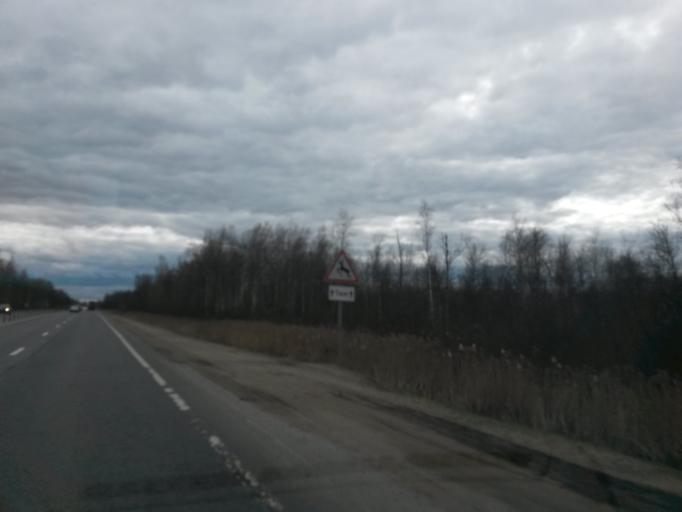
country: RU
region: Jaroslavl
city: Rostov
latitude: 57.2338
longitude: 39.4699
